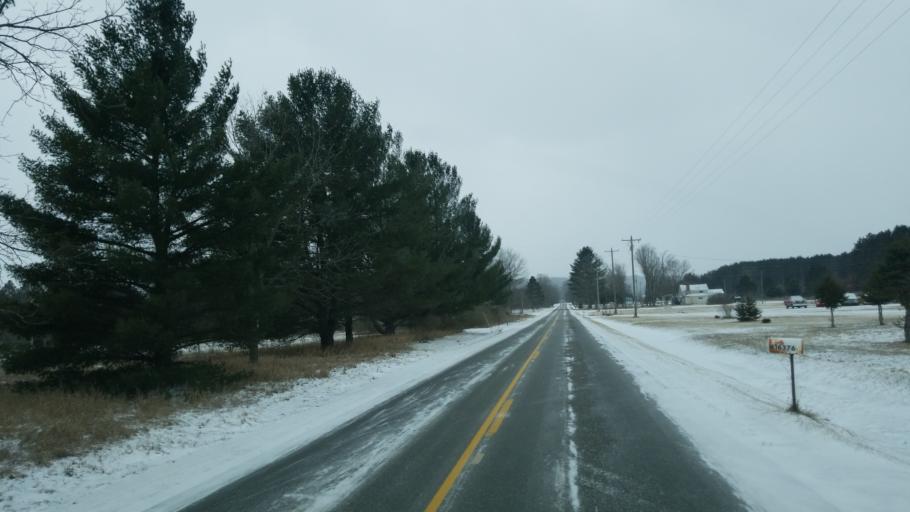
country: US
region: Michigan
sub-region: Osceola County
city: Reed City
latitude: 43.8218
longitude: -85.4114
